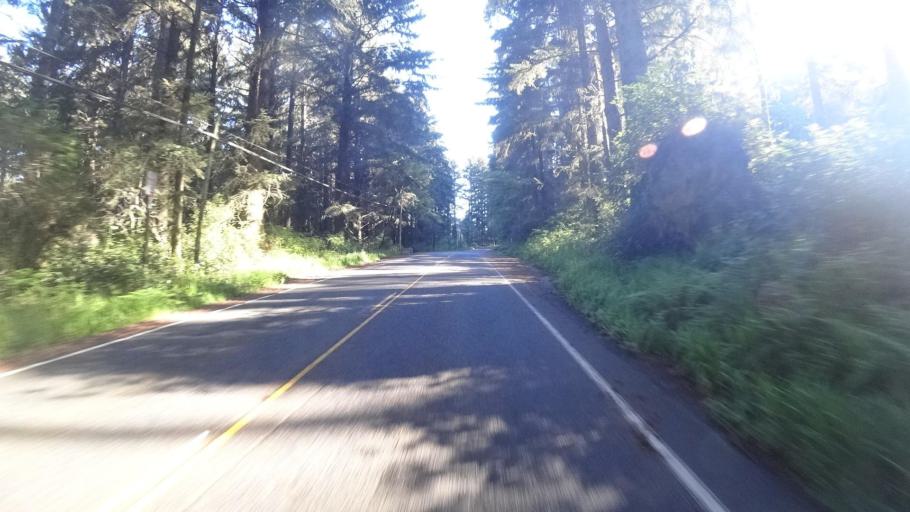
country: US
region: California
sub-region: Humboldt County
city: Westhaven-Moonstone
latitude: 41.1327
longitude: -124.1532
